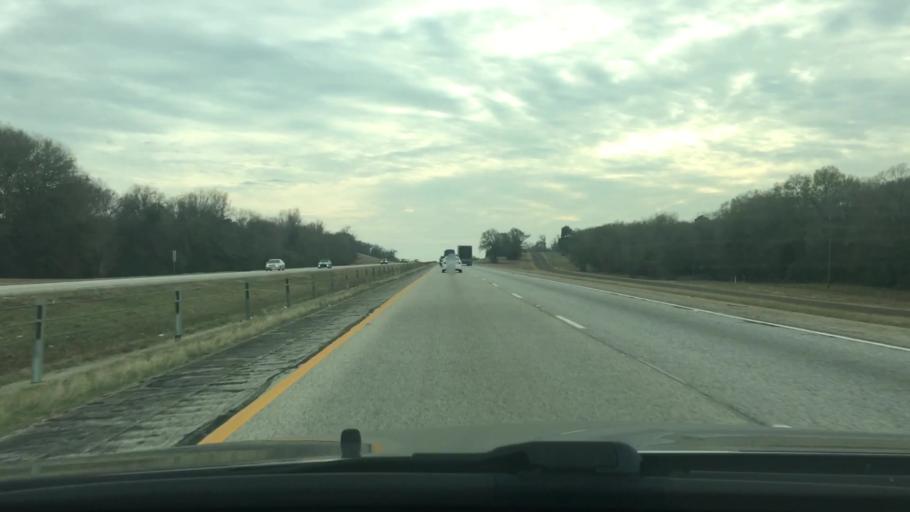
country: US
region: Texas
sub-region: Leon County
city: Centerville
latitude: 31.2294
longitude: -95.9948
